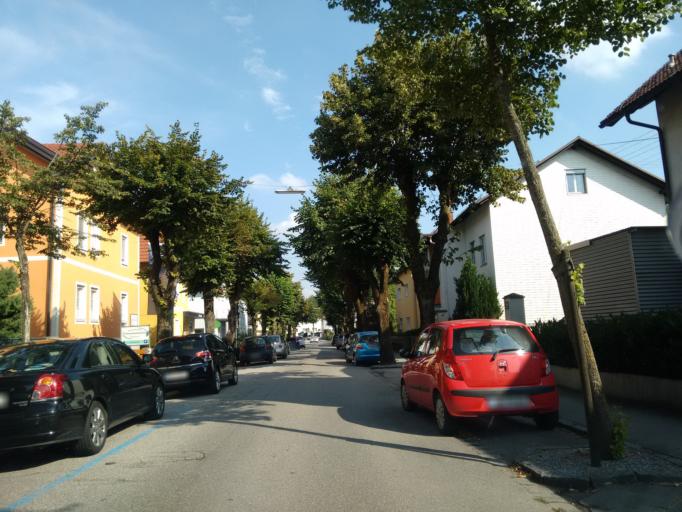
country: AT
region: Upper Austria
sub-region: Politischer Bezirk Grieskirchen
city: Grieskirchen
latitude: 48.2340
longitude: 13.8319
